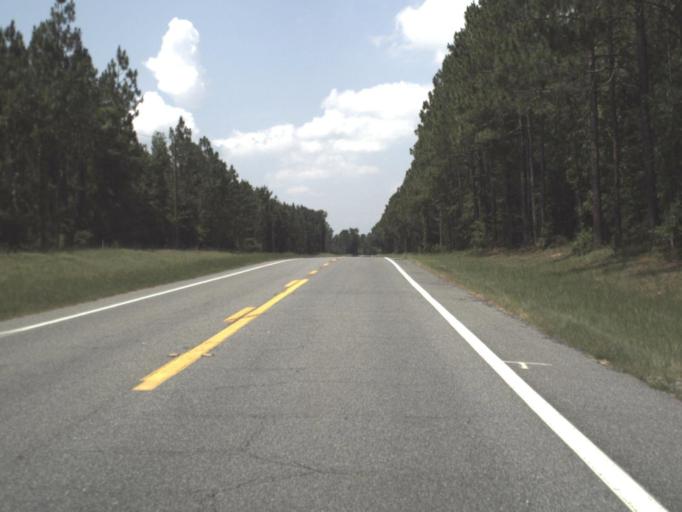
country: US
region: Florida
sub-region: Hamilton County
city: Jasper
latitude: 30.4979
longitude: -83.0747
